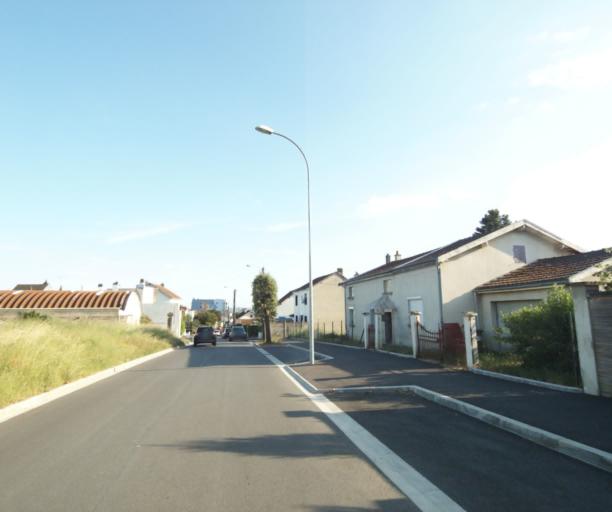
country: FR
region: Champagne-Ardenne
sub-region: Departement des Ardennes
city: Charleville-Mezieres
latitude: 49.7888
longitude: 4.7097
